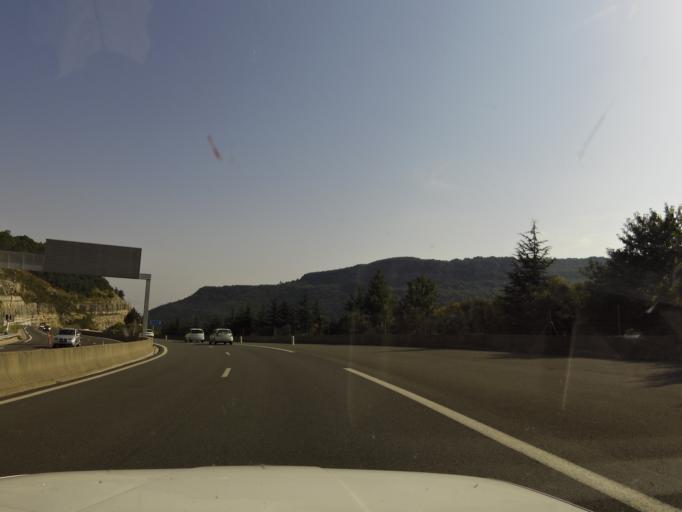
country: FR
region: Languedoc-Roussillon
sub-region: Departement de l'Herault
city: Lodeve
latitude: 43.8203
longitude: 3.3187
